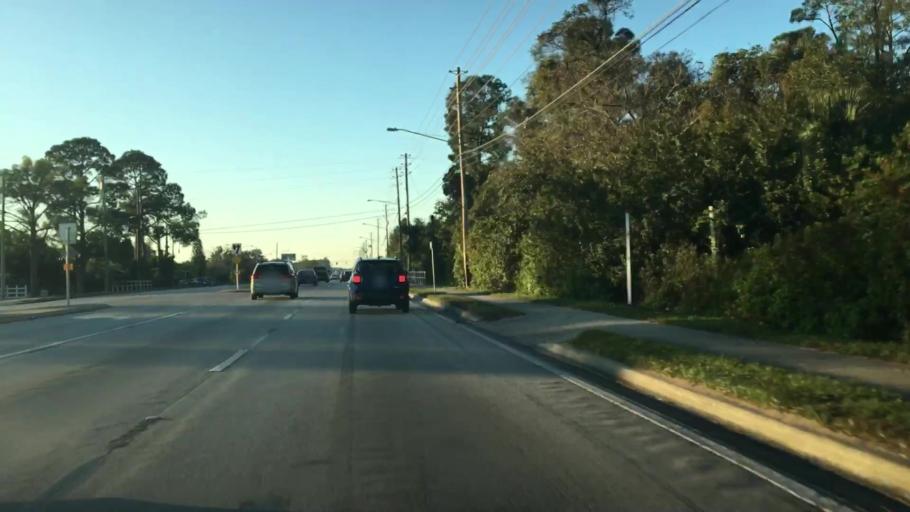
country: US
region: Florida
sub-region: Orange County
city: Conway
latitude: 28.4961
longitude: -81.2855
